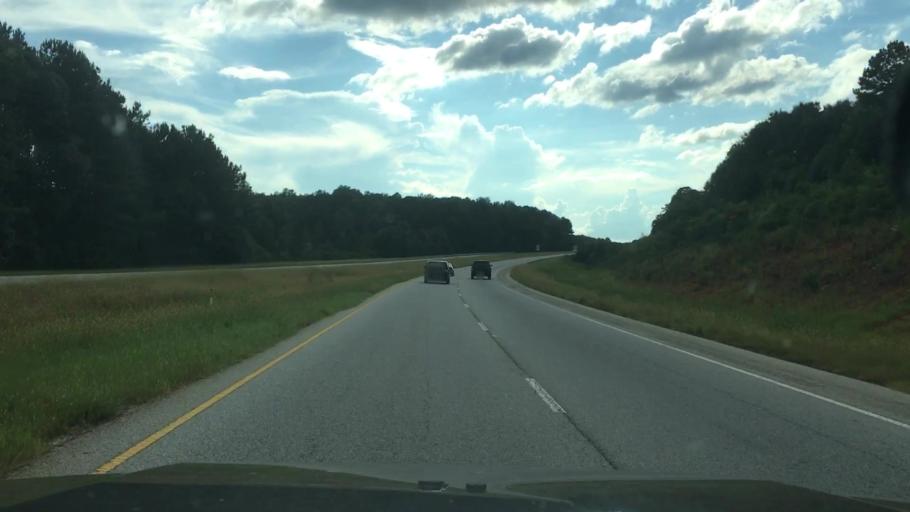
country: US
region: Georgia
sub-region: Spalding County
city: East Griffin
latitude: 33.2366
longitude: -84.1732
